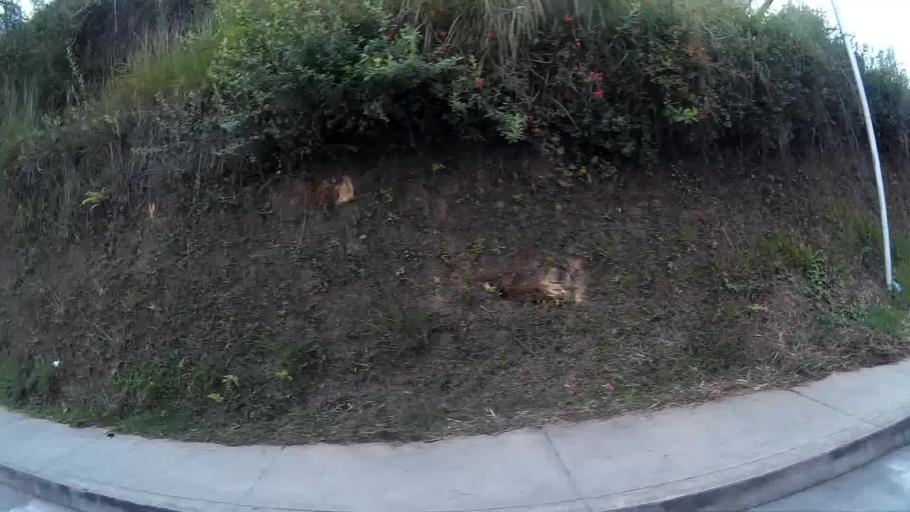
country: CO
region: Risaralda
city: Pereira
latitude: 4.8063
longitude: -75.7311
